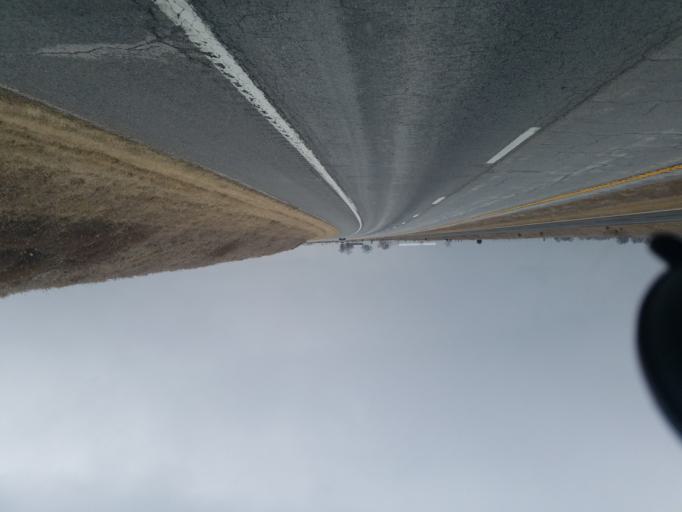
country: US
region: Missouri
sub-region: Macon County
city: La Plata
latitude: 39.8887
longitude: -92.4710
